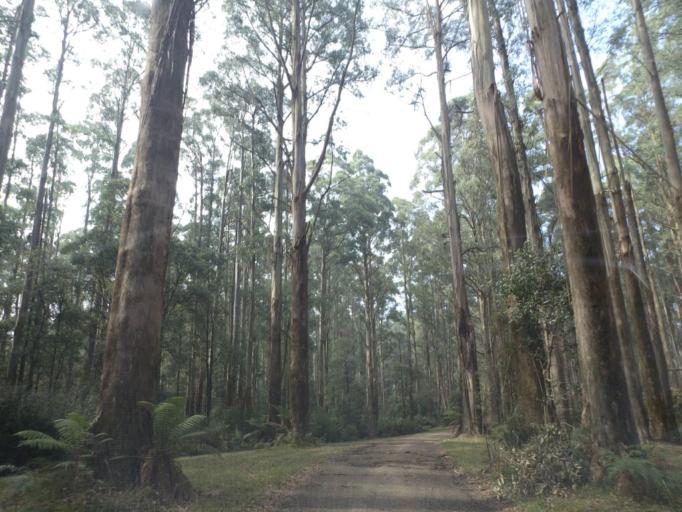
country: AU
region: Victoria
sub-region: Yarra Ranges
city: Healesville
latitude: -37.5803
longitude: 145.5521
